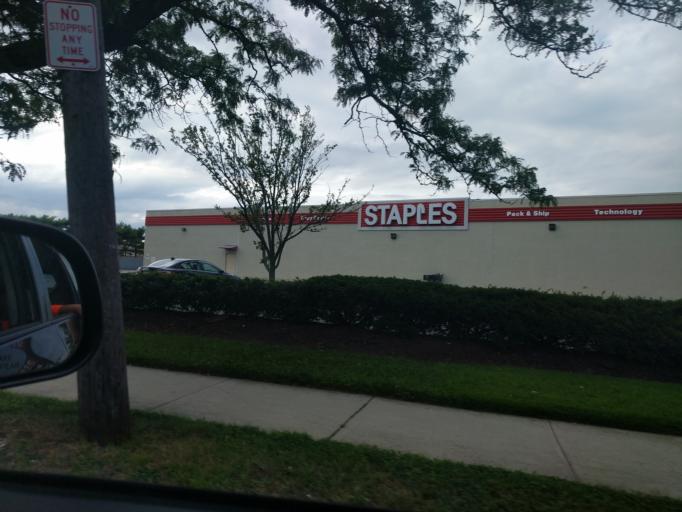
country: US
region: New York
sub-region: Nassau County
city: Barnum Island
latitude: 40.6207
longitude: -73.6426
